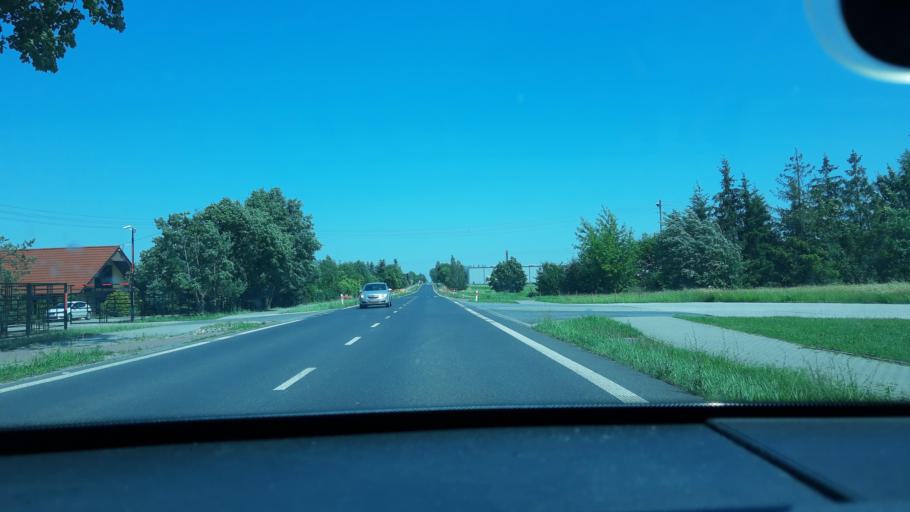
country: PL
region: Lodz Voivodeship
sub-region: Powiat zdunskowolski
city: Zapolice
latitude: 51.6055
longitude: 18.8543
